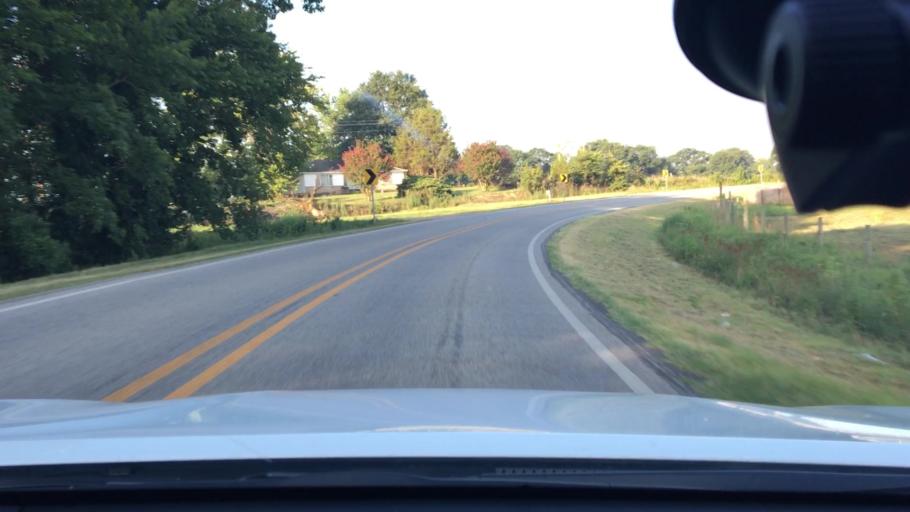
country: US
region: Arkansas
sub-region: Johnson County
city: Coal Hill
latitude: 35.3512
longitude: -93.5668
